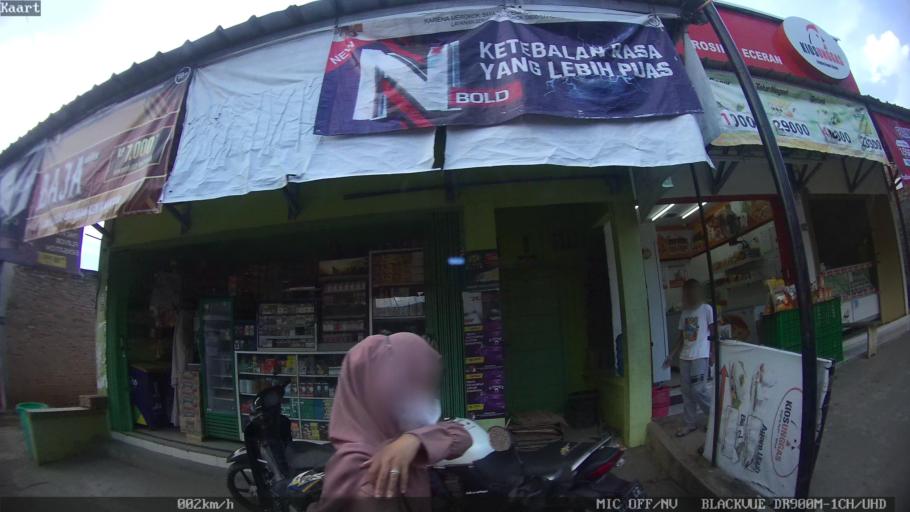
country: ID
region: Lampung
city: Kedaton
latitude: -5.3936
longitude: 105.2013
